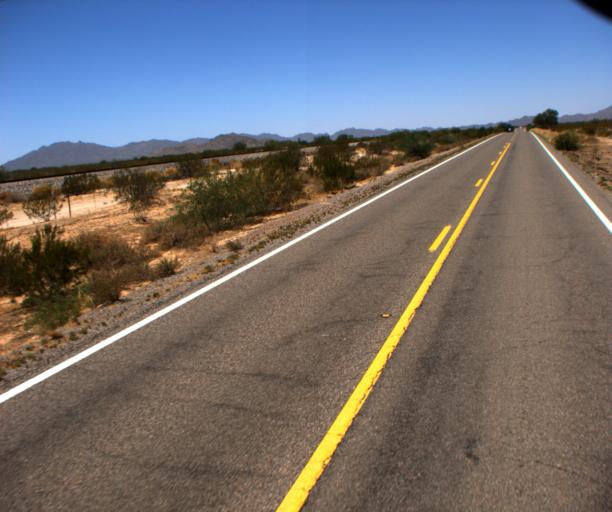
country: US
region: Arizona
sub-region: Pinal County
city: Maricopa
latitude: 33.0424
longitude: -112.3231
